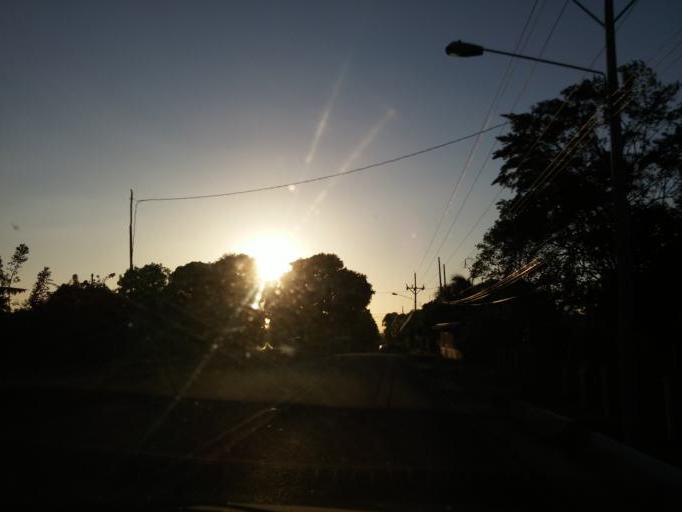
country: CR
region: Alajuela
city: Orotina
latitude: 9.9149
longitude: -84.5360
